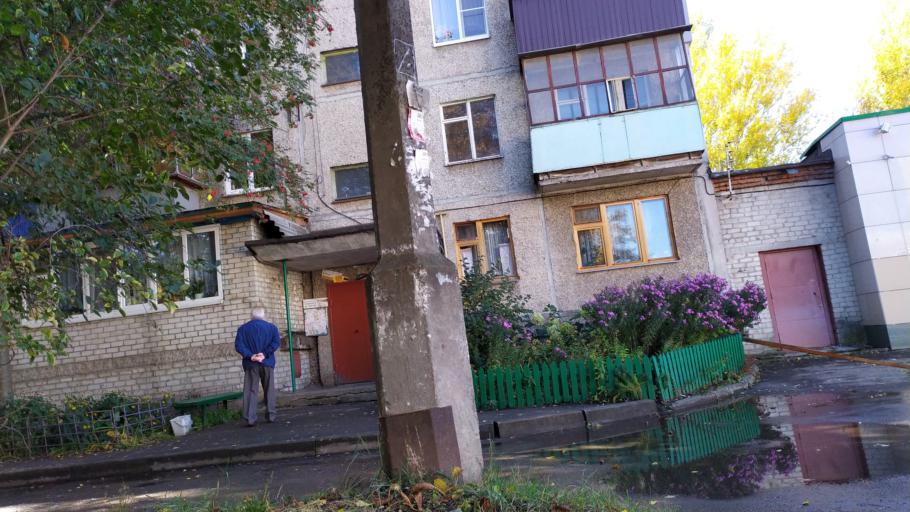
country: RU
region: Kursk
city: Kursk
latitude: 51.6513
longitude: 36.1403
